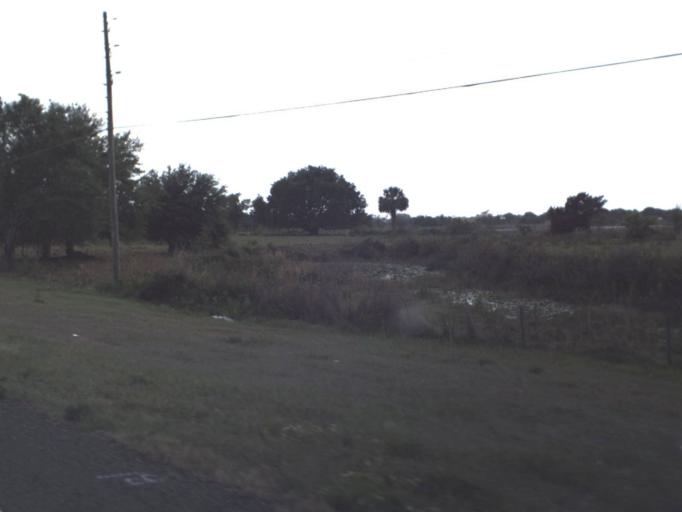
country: US
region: Florida
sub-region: Lake County
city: Yalaha
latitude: 28.6955
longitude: -81.8570
